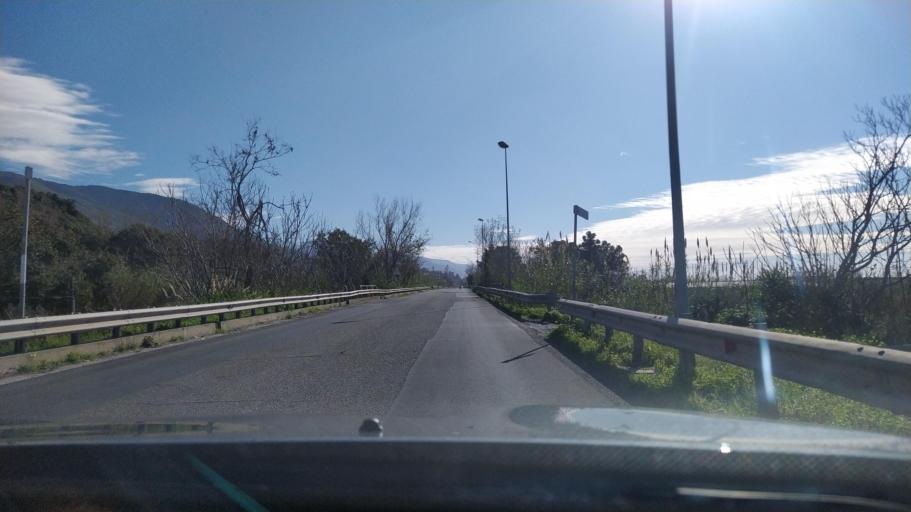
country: IT
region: Calabria
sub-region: Provincia di Cosenza
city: Paola
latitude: 39.3790
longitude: 16.0249
